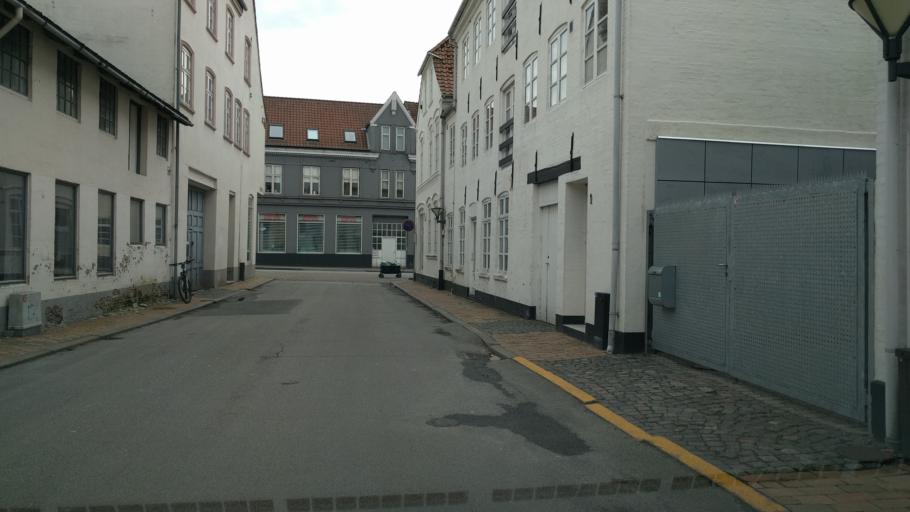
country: DK
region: South Denmark
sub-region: Haderslev Kommune
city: Haderslev
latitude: 55.2527
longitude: 9.4821
